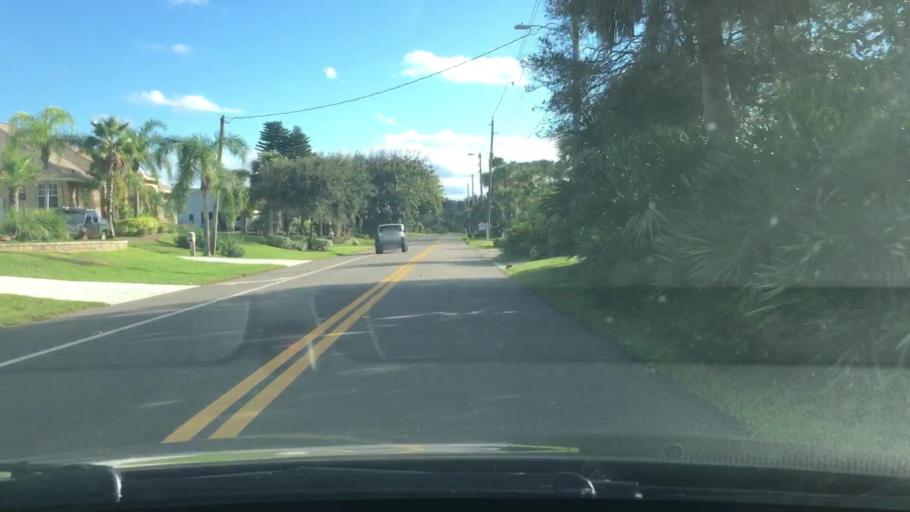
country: US
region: Florida
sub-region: Volusia County
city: Ormond-by-the-Sea
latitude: 29.3805
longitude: -81.0864
